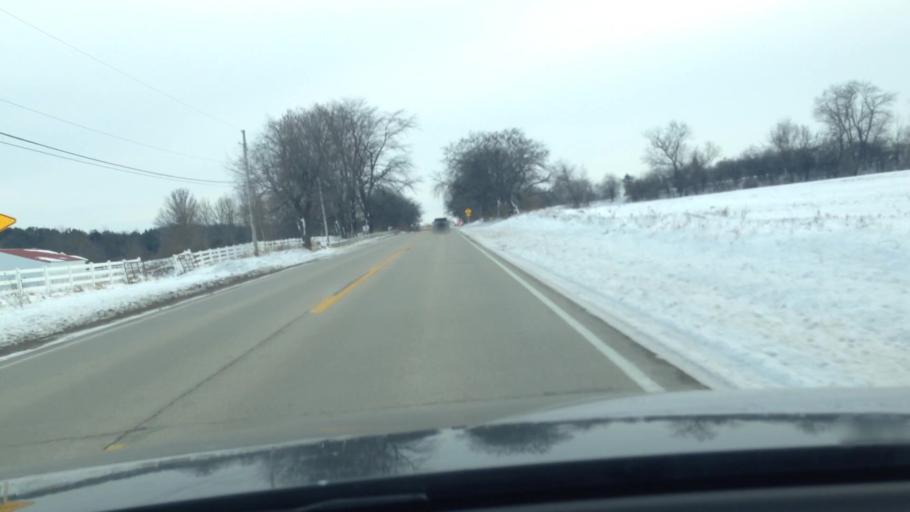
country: US
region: Illinois
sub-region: McHenry County
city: Woodstock
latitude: 42.3651
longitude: -88.4432
